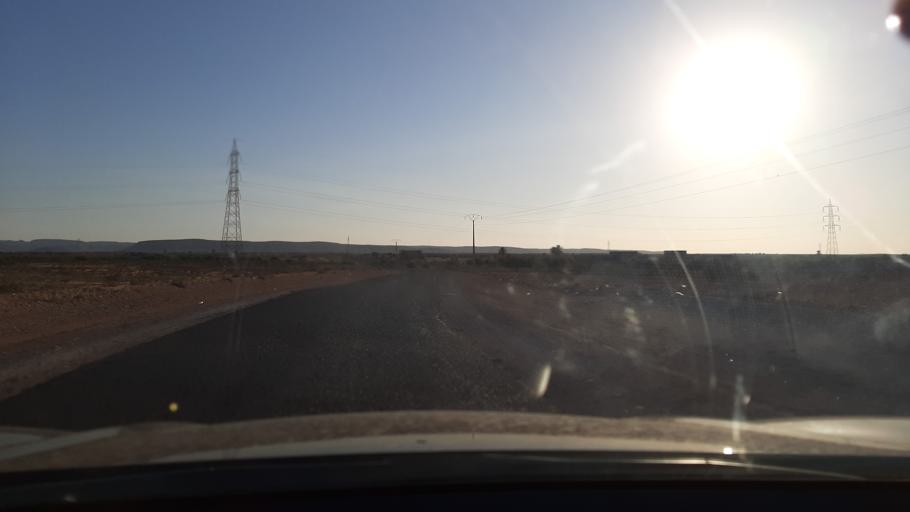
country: TN
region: Qabis
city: Matmata
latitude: 33.6162
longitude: 10.2337
